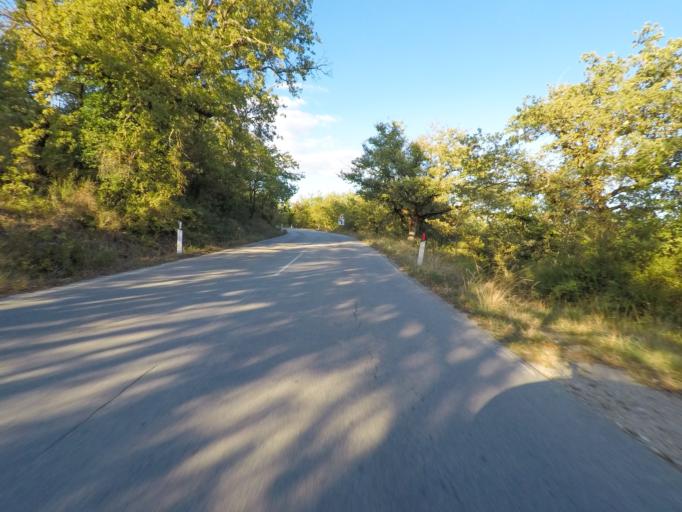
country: IT
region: Tuscany
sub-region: Provincia di Siena
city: Radda in Chianti
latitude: 43.4493
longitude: 11.3915
